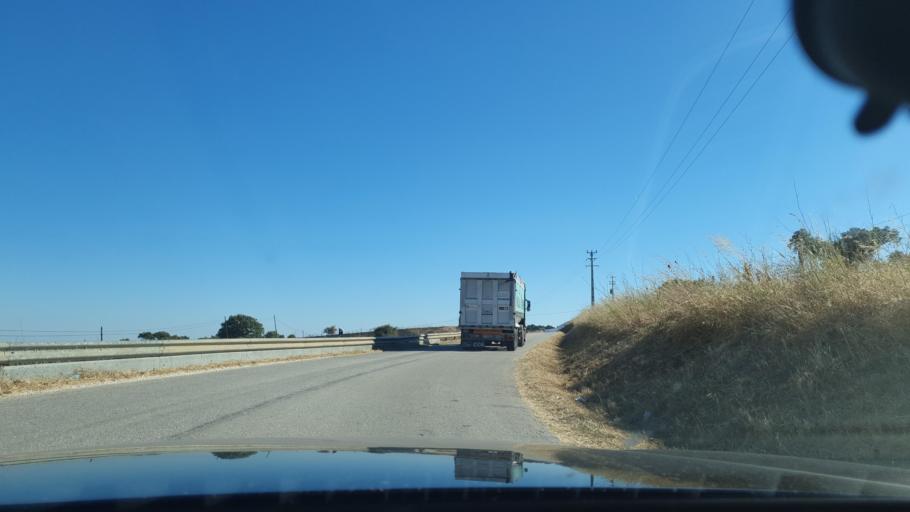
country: PT
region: Evora
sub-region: Alandroal
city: Alandroal
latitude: 38.7280
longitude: -7.4049
